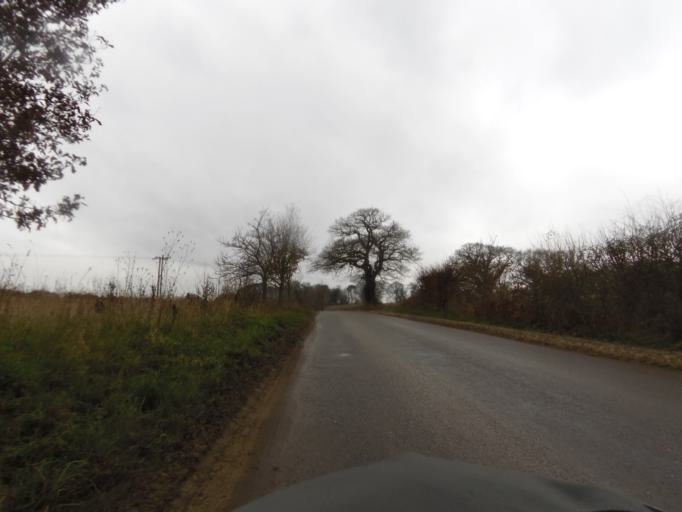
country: GB
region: England
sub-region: Norfolk
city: Briston
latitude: 52.8804
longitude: 1.0785
